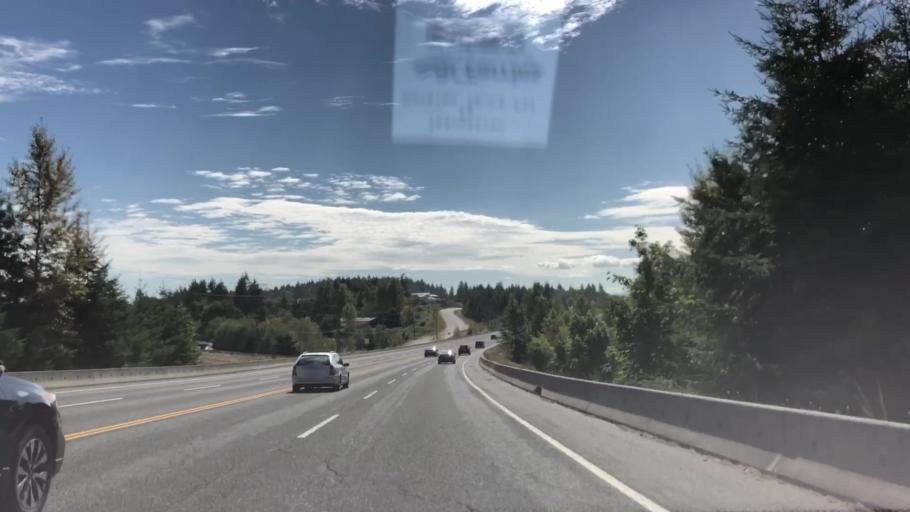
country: CA
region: British Columbia
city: Nanaimo
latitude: 49.1307
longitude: -123.8658
